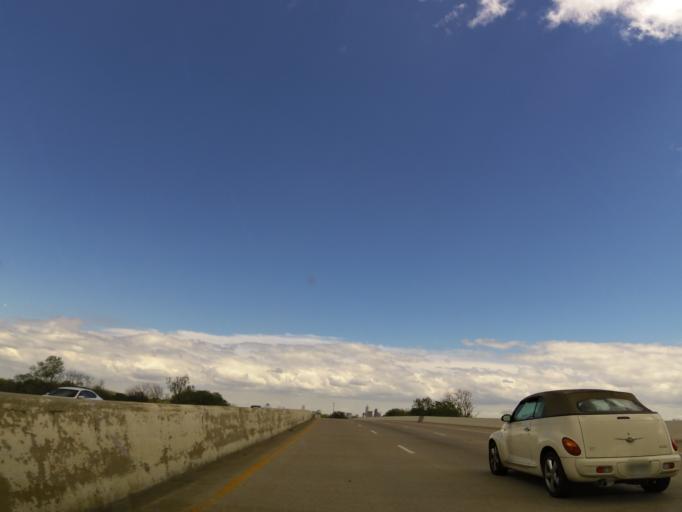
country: US
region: Tennessee
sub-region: Shelby County
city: Memphis
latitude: 35.1531
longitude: -90.1019
